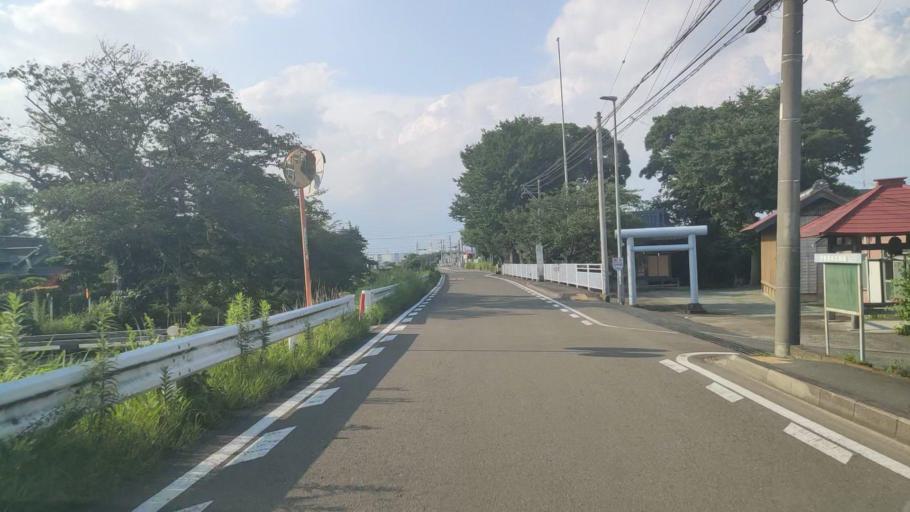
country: JP
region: Kanagawa
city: Isehara
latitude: 35.3887
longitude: 139.3385
